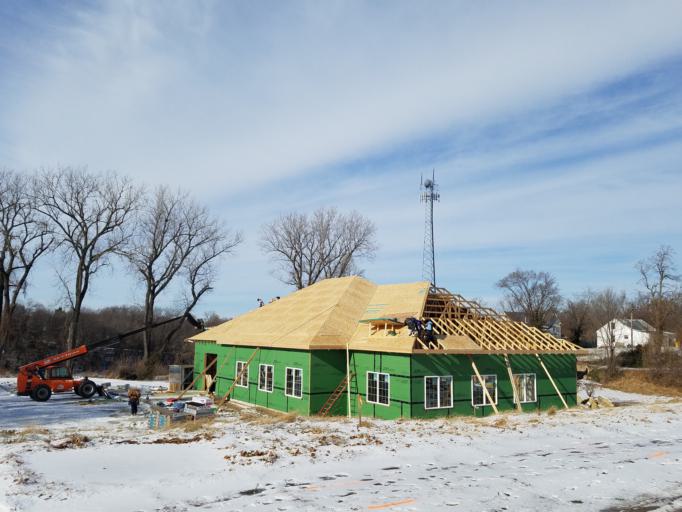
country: US
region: Missouri
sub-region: Lafayette County
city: Lexington
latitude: 39.1857
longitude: -93.8764
